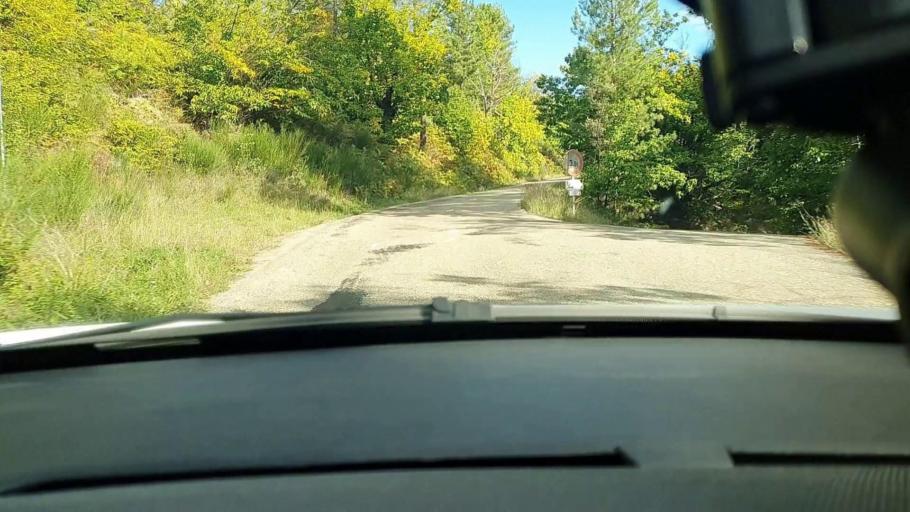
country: FR
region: Languedoc-Roussillon
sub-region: Departement du Gard
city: Besseges
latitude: 44.3739
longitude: 3.9910
